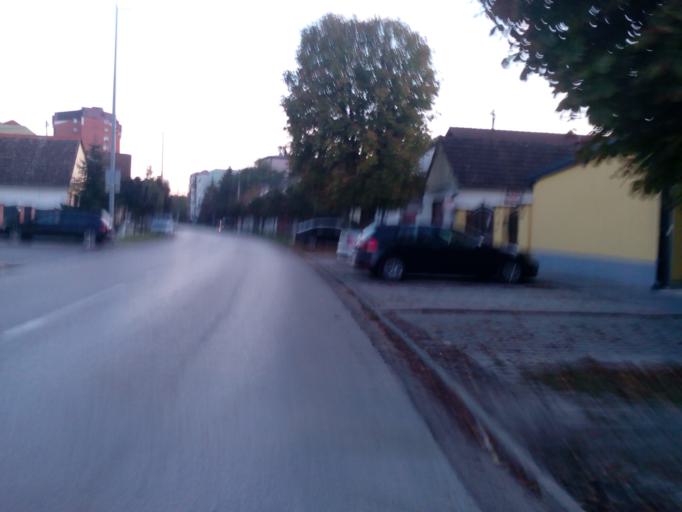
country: HR
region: Vukovarsko-Srijemska
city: Vinkovci
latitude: 45.2956
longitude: 18.8038
